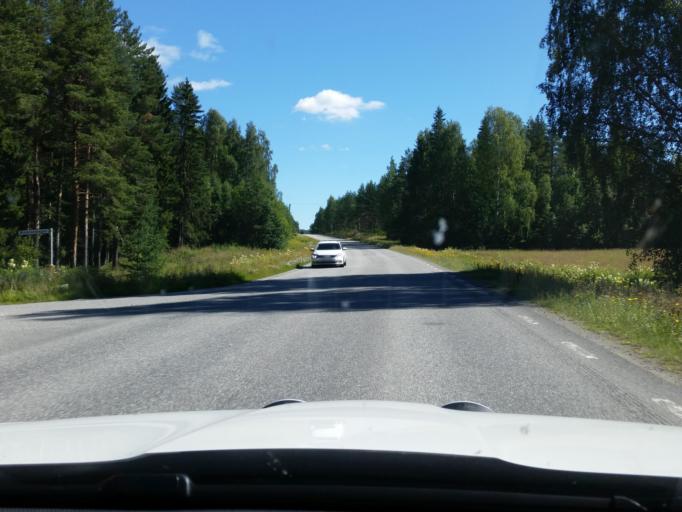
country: SE
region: Norrbotten
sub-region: Pitea Kommun
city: Bergsviken
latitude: 65.3158
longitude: 21.2990
